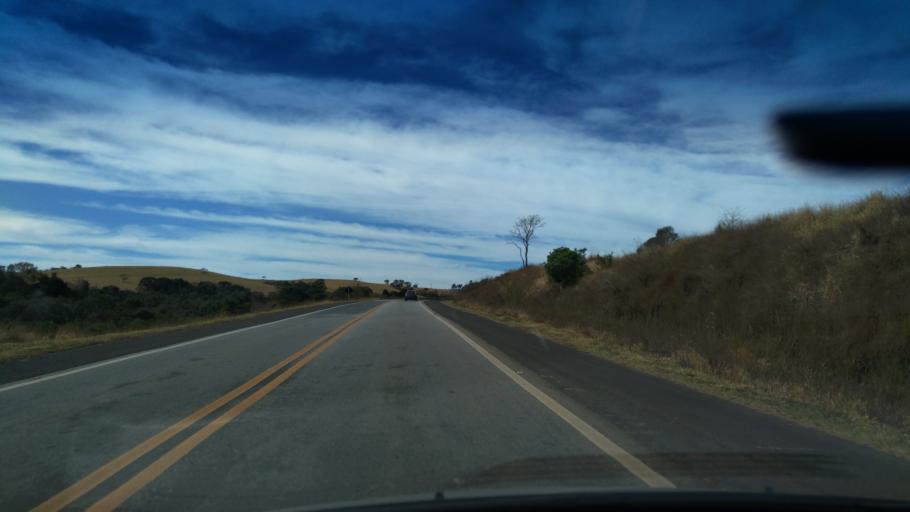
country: BR
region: Minas Gerais
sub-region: Borda Da Mata
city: Borda da Mata
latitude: -22.0649
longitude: -46.2746
